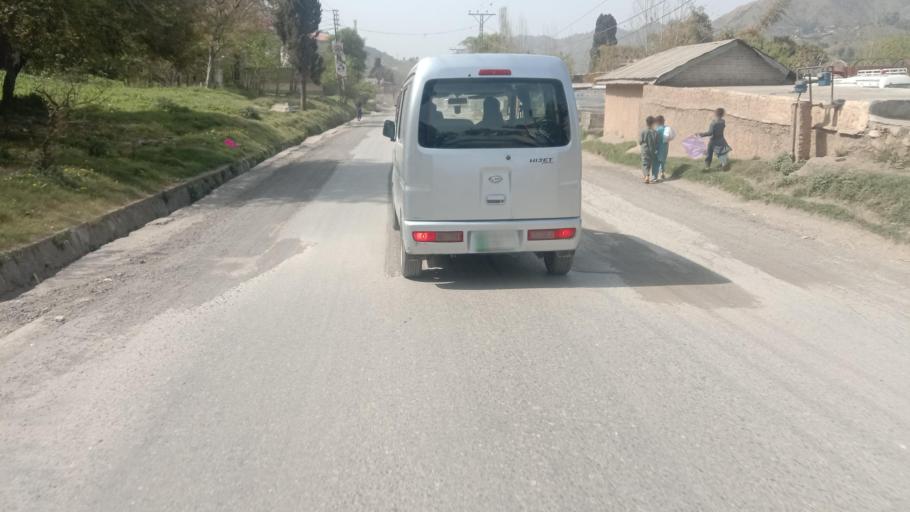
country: PK
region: Khyber Pakhtunkhwa
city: Abbottabad
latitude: 34.1331
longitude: 73.2028
